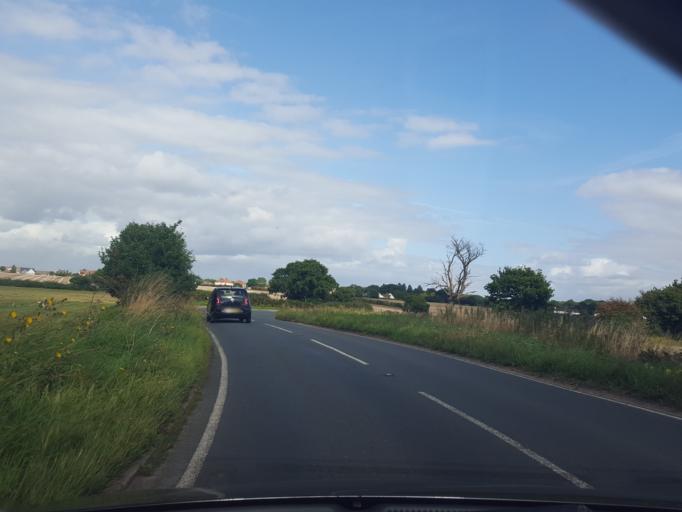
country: GB
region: England
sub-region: Essex
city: Mistley
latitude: 51.9330
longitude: 1.1668
